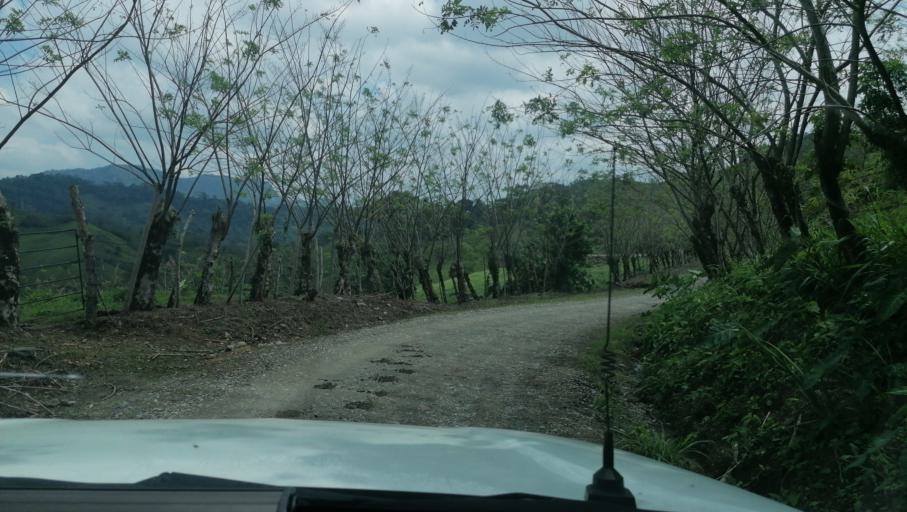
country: MX
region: Chiapas
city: Ixtacomitan
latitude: 17.4399
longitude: -93.2036
